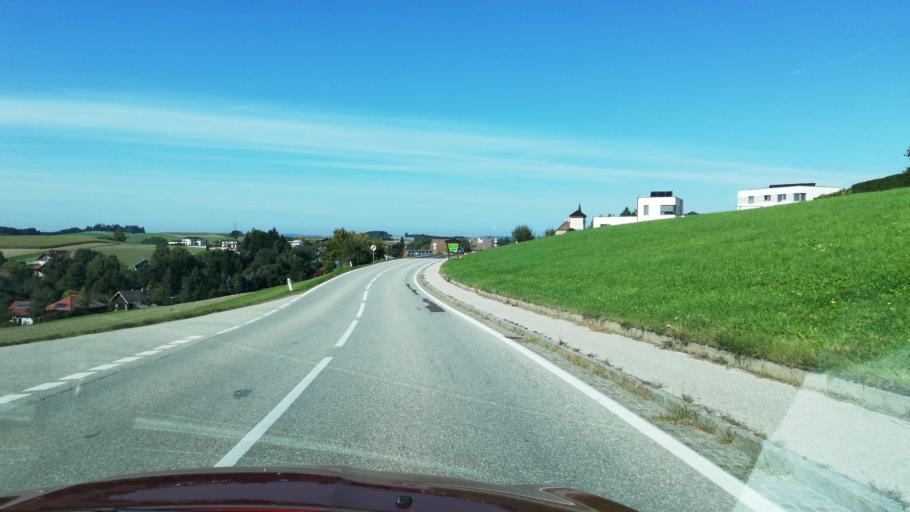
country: AT
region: Upper Austria
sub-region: Politischer Bezirk Vocklabruck
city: Redleiten
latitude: 48.1514
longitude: 13.5638
